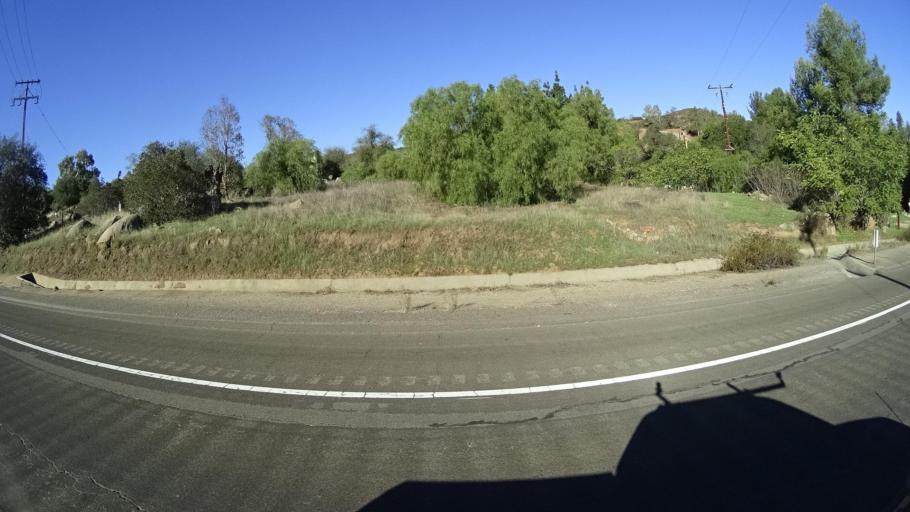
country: MX
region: Baja California
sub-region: Tijuana
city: Villa del Campo
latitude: 32.6296
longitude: -116.7643
